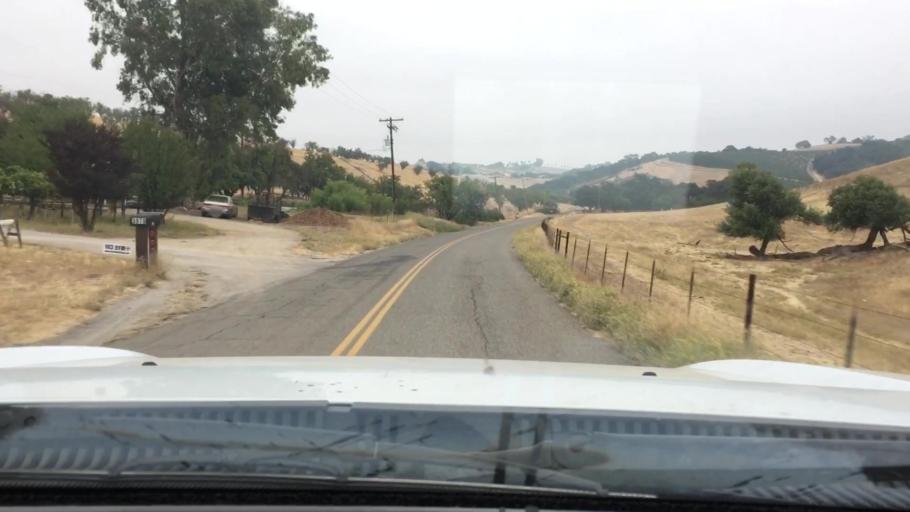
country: US
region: California
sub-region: San Luis Obispo County
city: Atascadero
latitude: 35.5306
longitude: -120.6270
